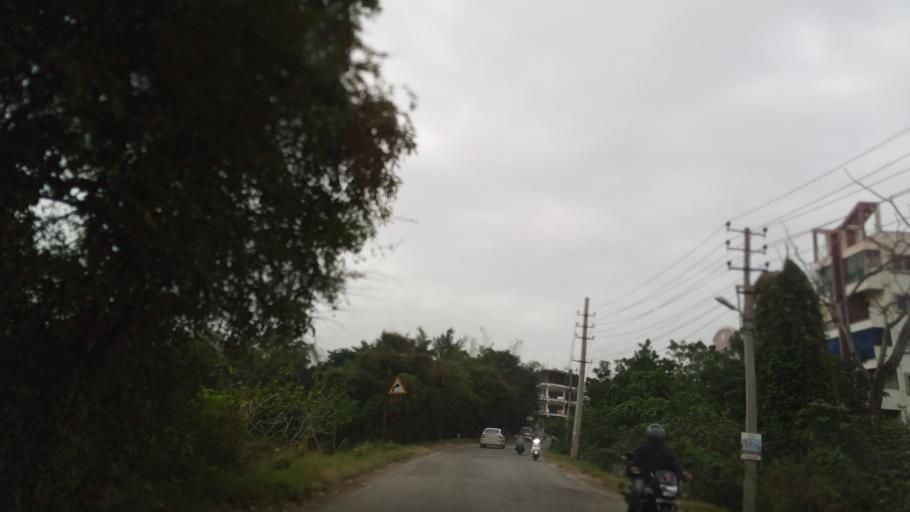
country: IN
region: Karnataka
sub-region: Bangalore Urban
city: Bangalore
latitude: 12.9090
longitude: 77.4922
